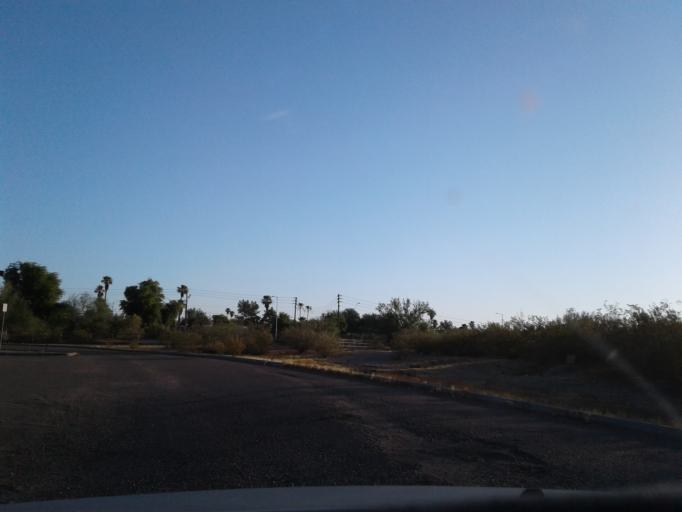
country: US
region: Arizona
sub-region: Maricopa County
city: Glendale
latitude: 33.6242
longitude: -112.0974
